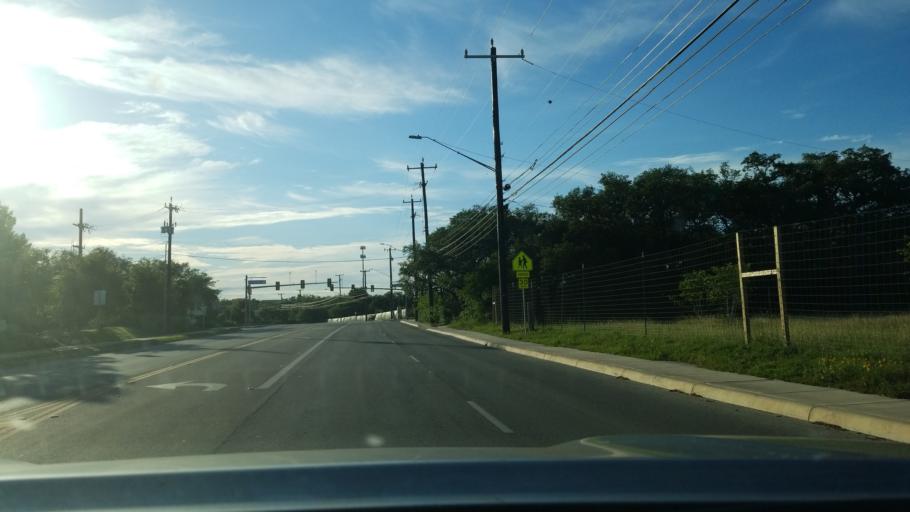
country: US
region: Texas
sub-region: Bexar County
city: Hollywood Park
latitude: 29.6183
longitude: -98.4569
